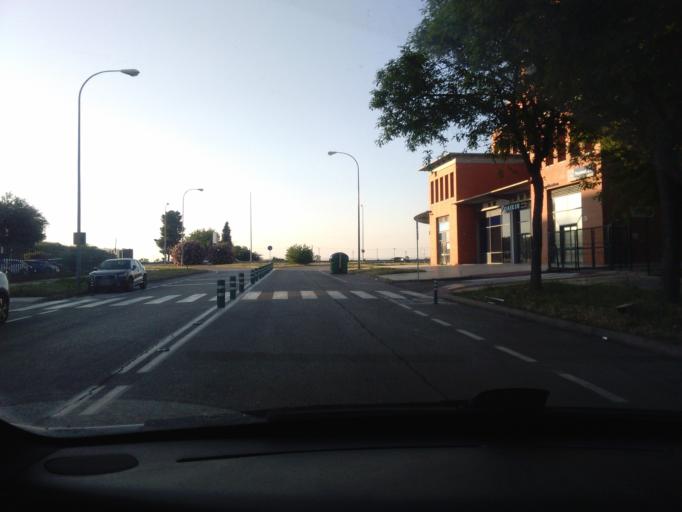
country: ES
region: Andalusia
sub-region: Provincia de Sevilla
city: Sevilla
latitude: 37.4078
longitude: -5.9452
